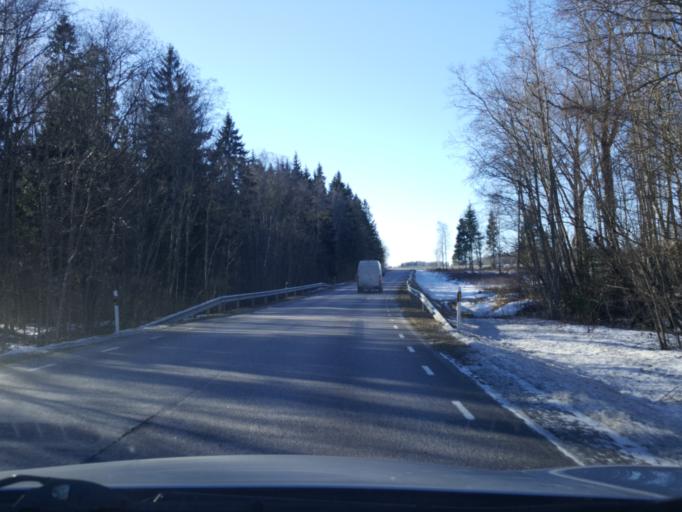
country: EE
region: Viljandimaa
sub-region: Viiratsi vald
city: Viiratsi
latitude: 58.4166
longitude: 25.6747
